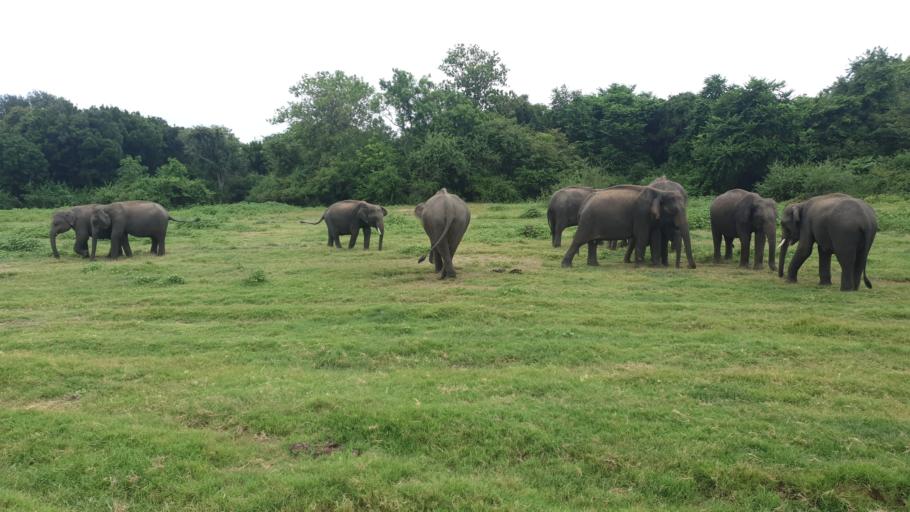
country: LK
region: North Central
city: Polonnaruwa
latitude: 8.1338
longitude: 80.9077
